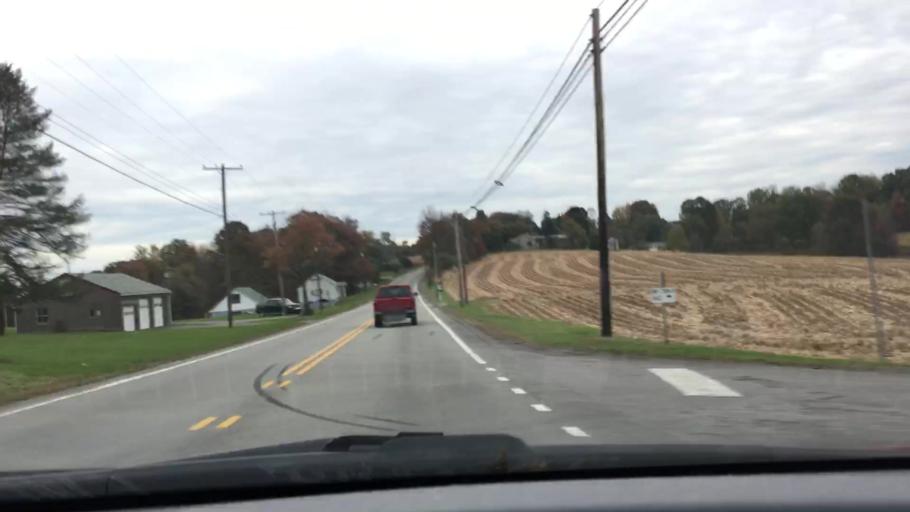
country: US
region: Pennsylvania
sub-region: Armstrong County
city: Orchard Hills
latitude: 40.6239
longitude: -79.4460
